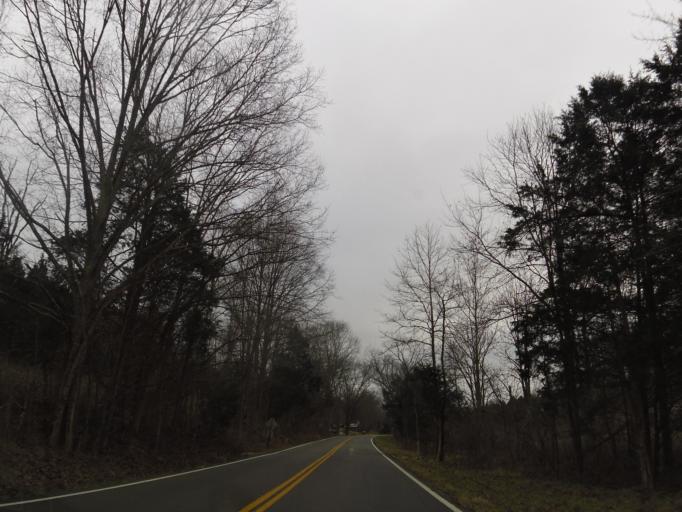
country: US
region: Kentucky
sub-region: Franklin County
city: Frankfort
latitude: 38.2845
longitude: -84.9439
